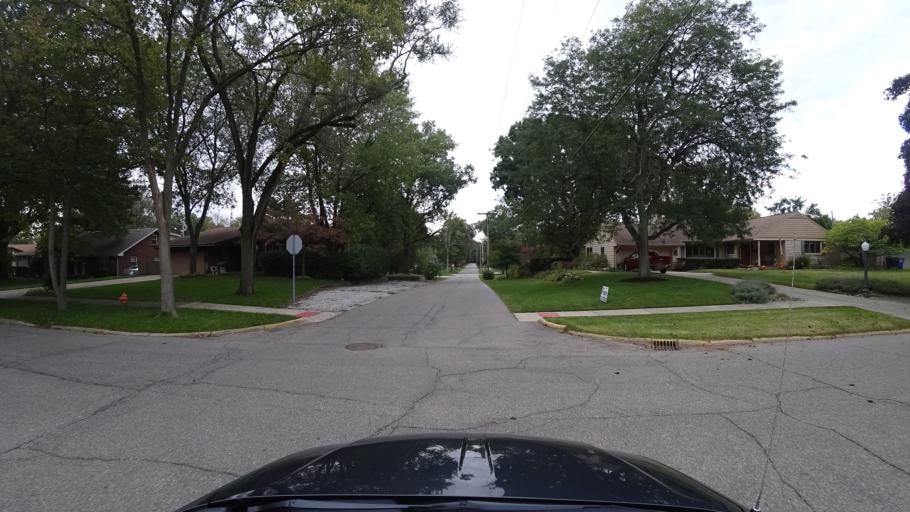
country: US
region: Indiana
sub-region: LaPorte County
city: Michigan City
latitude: 41.6986
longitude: -86.8904
